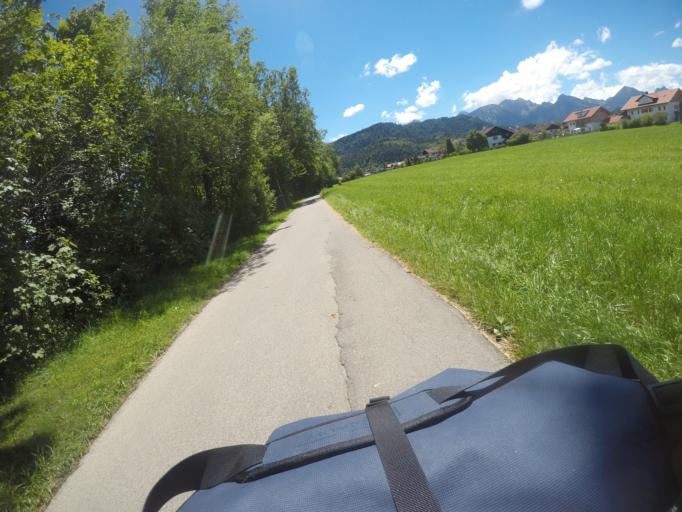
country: DE
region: Bavaria
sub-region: Swabia
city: Fuessen
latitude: 47.5753
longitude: 10.7121
